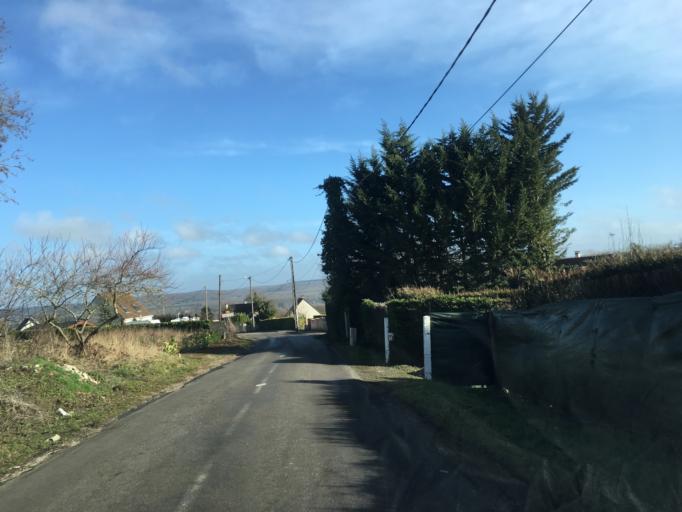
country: FR
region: Haute-Normandie
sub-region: Departement de l'Eure
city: Saint-Just
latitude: 49.1040
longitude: 1.4329
